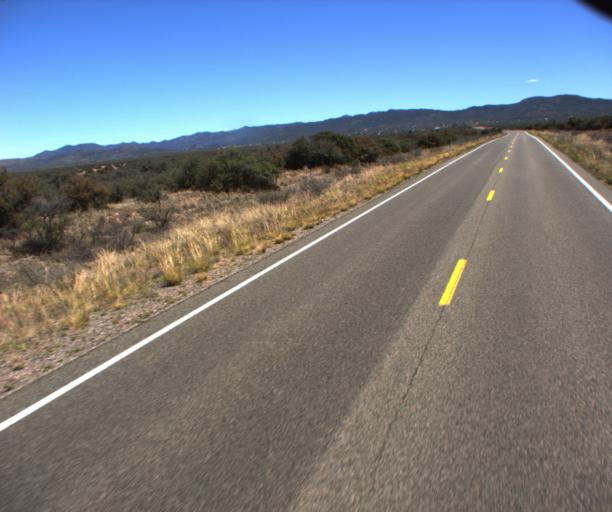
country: US
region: Arizona
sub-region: Yavapai County
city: Prescott
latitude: 34.3934
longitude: -112.6349
